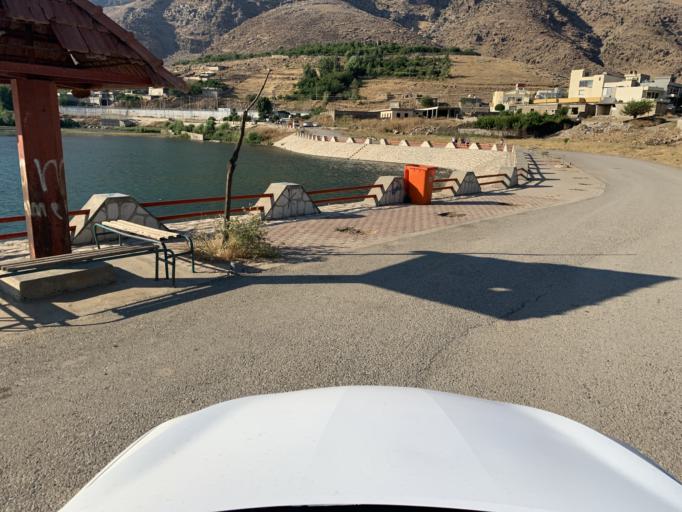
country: IQ
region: As Sulaymaniyah
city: Raniye
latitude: 36.2731
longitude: 44.7559
